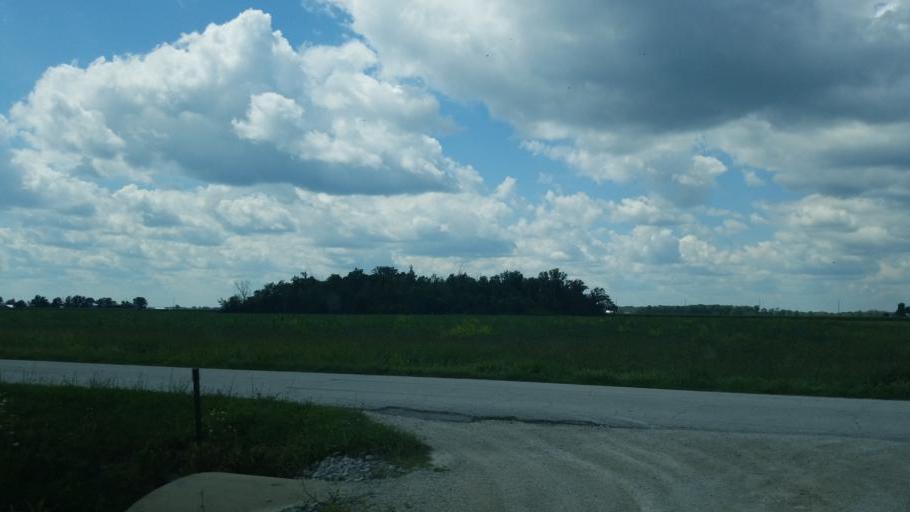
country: US
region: Ohio
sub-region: Sandusky County
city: Gibsonburg
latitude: 41.3938
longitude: -83.3385
